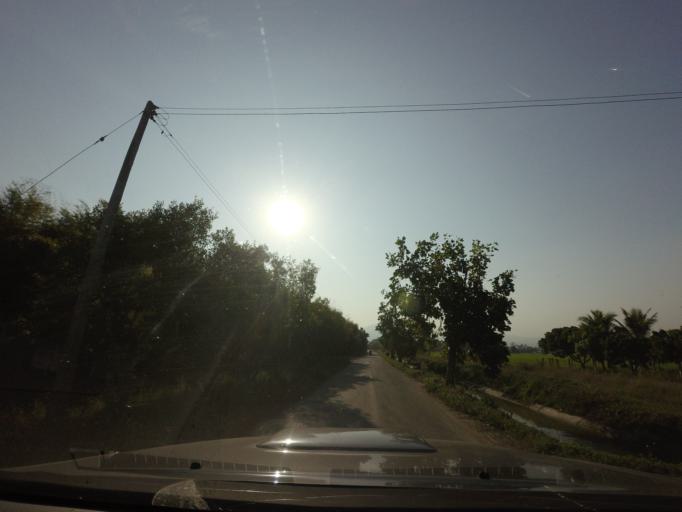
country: TH
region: Chiang Mai
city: San Sai
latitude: 18.9409
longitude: 98.9605
